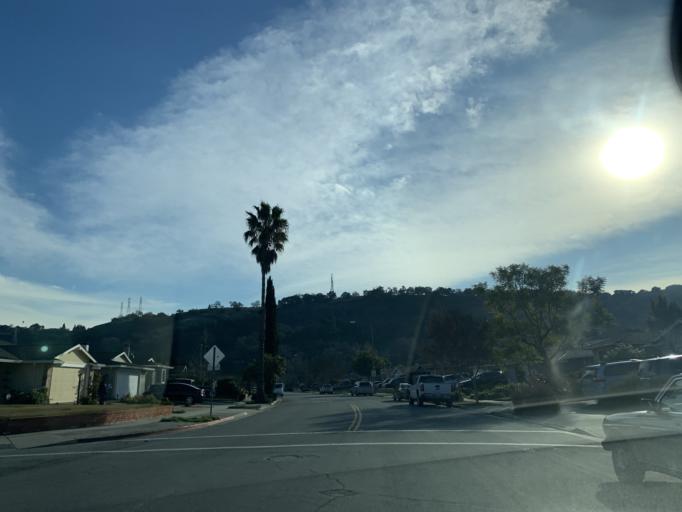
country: US
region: California
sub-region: Santa Clara County
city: Seven Trees
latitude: 37.2346
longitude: -121.8408
